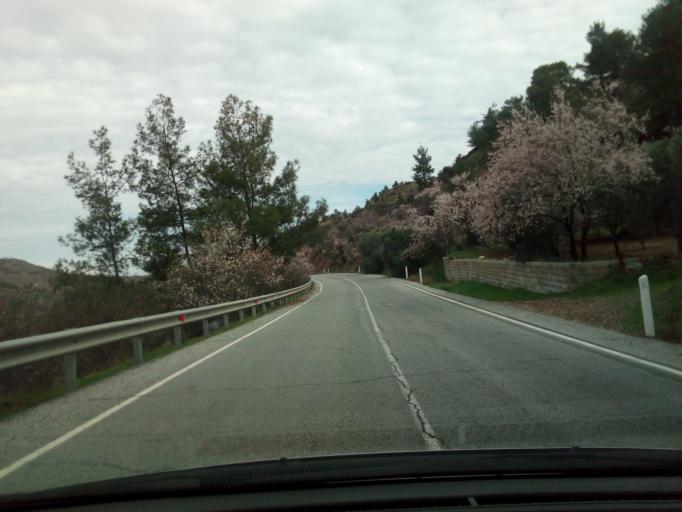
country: CY
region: Lefkosia
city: Klirou
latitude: 34.9631
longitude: 33.1492
